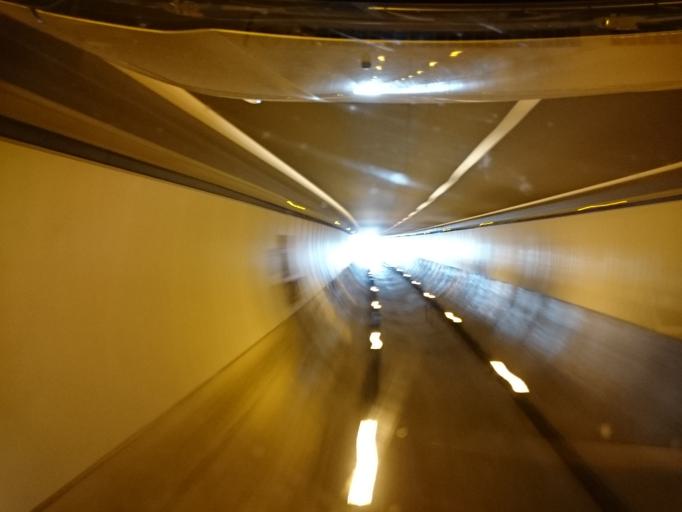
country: IT
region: Trentino-Alto Adige
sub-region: Bolzano
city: Fortezza
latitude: 46.7921
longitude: 11.6104
